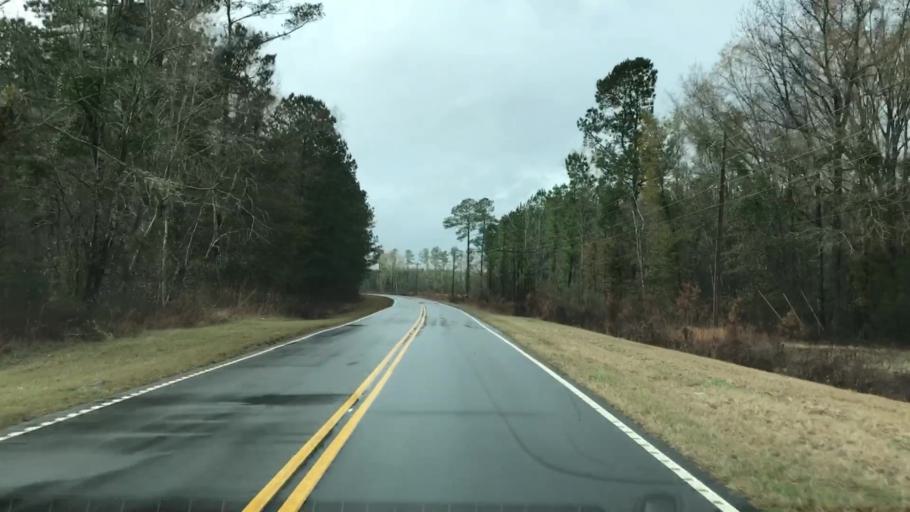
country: US
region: South Carolina
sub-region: Florence County
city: Johnsonville
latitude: 33.6757
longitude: -79.3346
